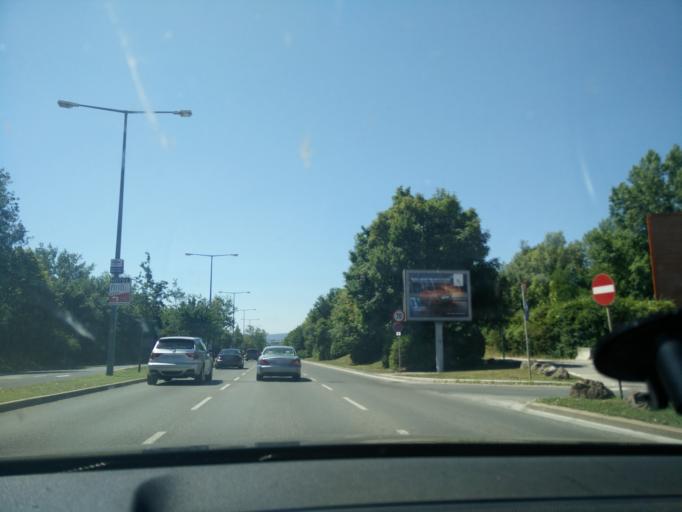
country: AT
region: Lower Austria
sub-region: Politischer Bezirk Modling
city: Vosendorf
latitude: 48.1654
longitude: 16.3471
